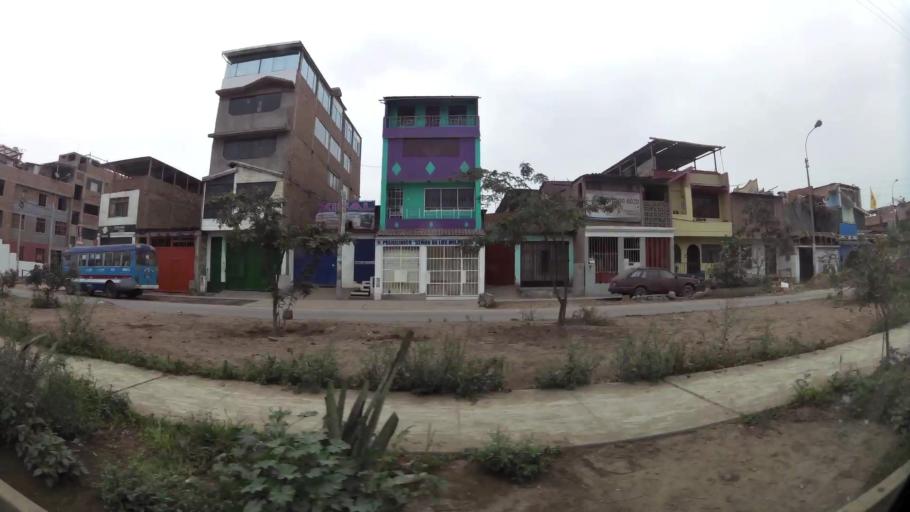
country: PE
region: Lima
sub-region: Lima
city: Surco
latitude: -12.2345
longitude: -76.9212
